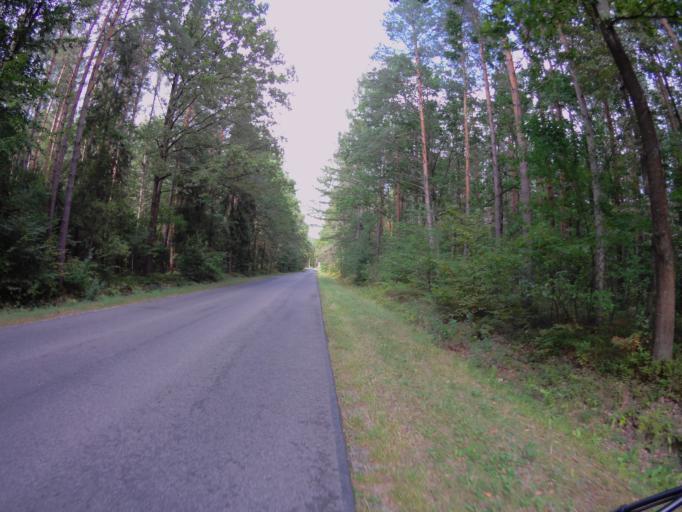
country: PL
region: Subcarpathian Voivodeship
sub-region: Powiat lezajski
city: Brzoza Krolewska
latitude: 50.2593
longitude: 22.3670
